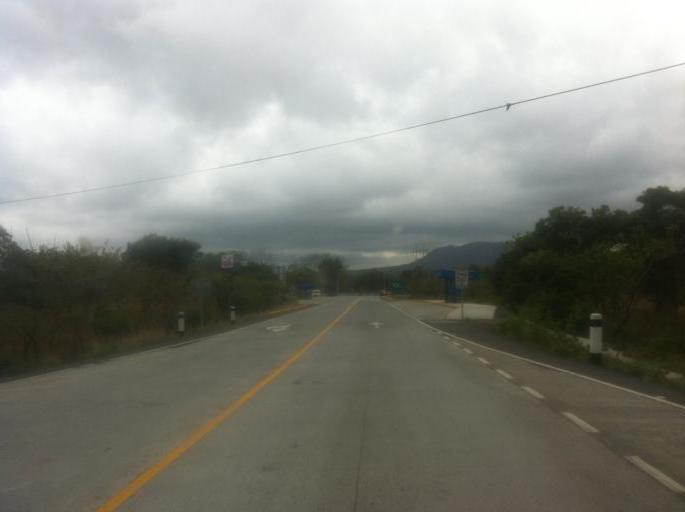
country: NI
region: Masaya
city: Nindiri
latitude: 11.9981
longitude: -86.1071
